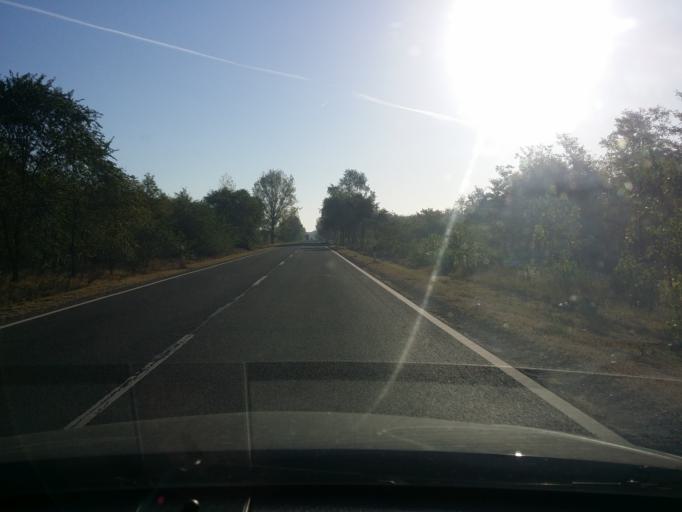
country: HU
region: Bacs-Kiskun
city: Nyarlorinc
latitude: 46.8638
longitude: 19.9190
